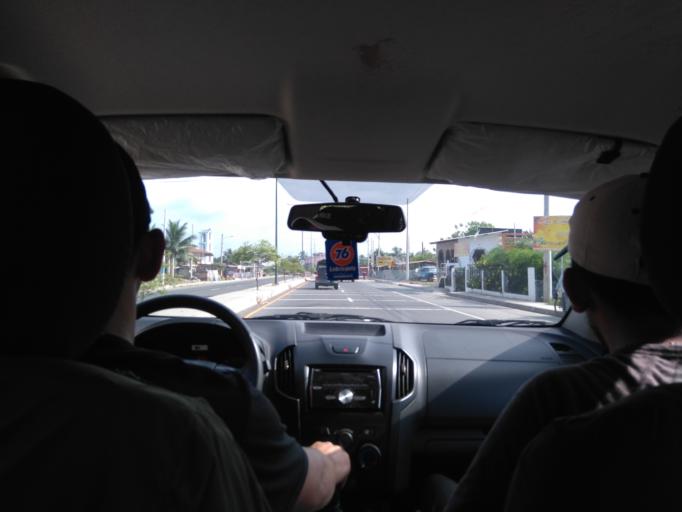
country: EC
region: Manabi
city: Rocafuerte
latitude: -0.9634
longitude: -80.4670
